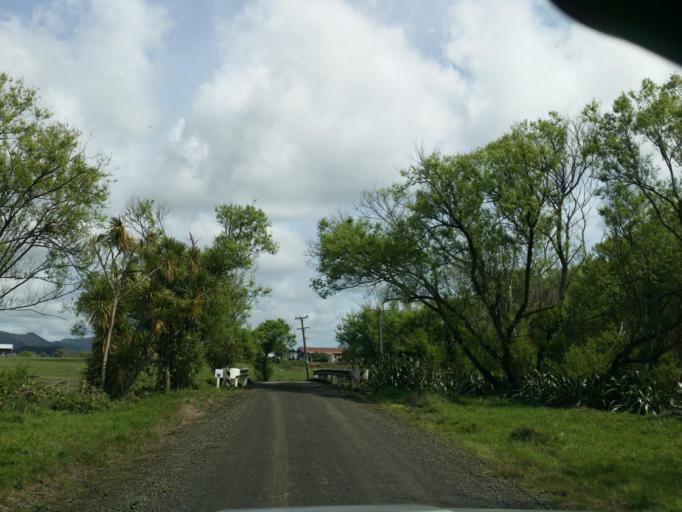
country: NZ
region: Northland
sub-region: Whangarei
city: Maungatapere
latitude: -35.8302
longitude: 174.0496
